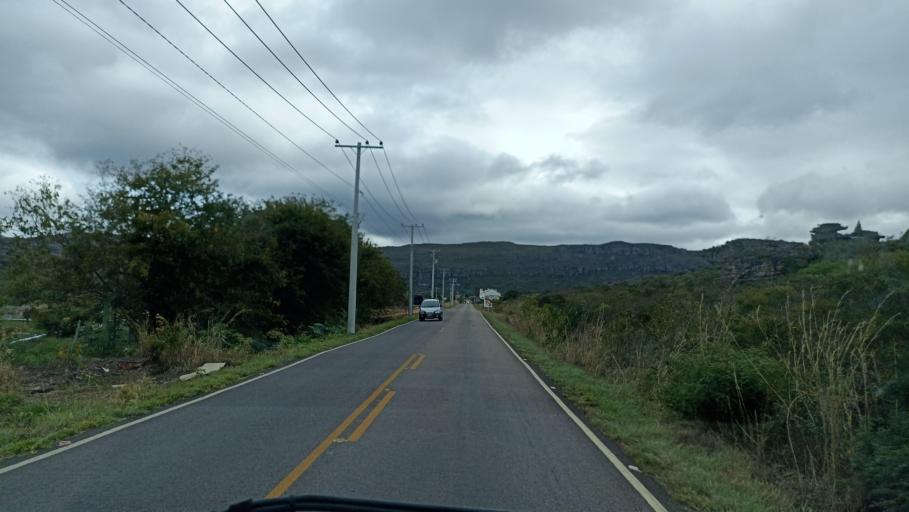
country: BR
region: Bahia
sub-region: Andarai
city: Vera Cruz
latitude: -12.9996
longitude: -41.3628
